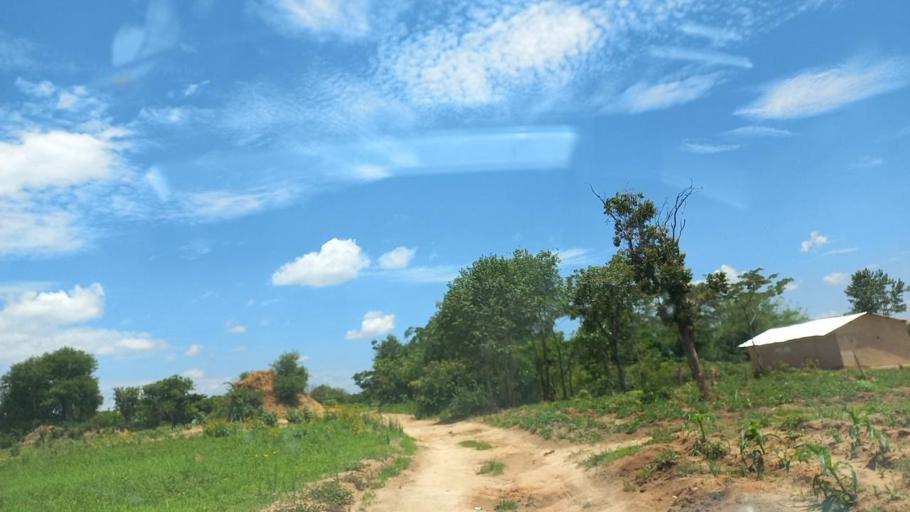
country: ZM
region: Copperbelt
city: Ndola
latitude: -12.8796
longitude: 28.4490
